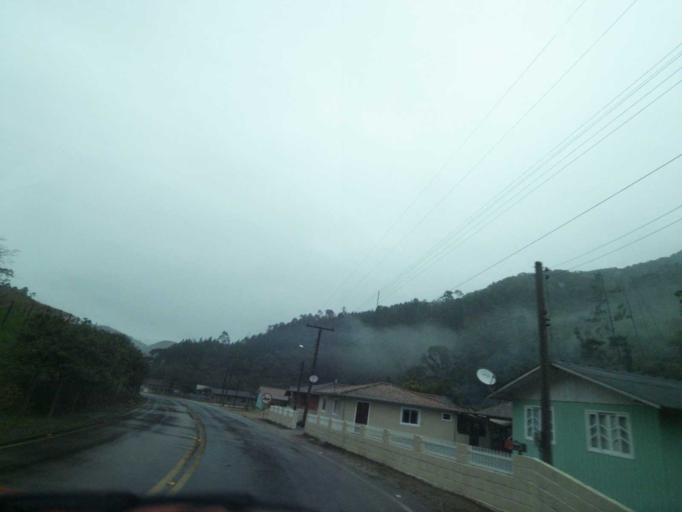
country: BR
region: Santa Catarina
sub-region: Anitapolis
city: Anitapolis
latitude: -27.8346
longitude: -49.0525
